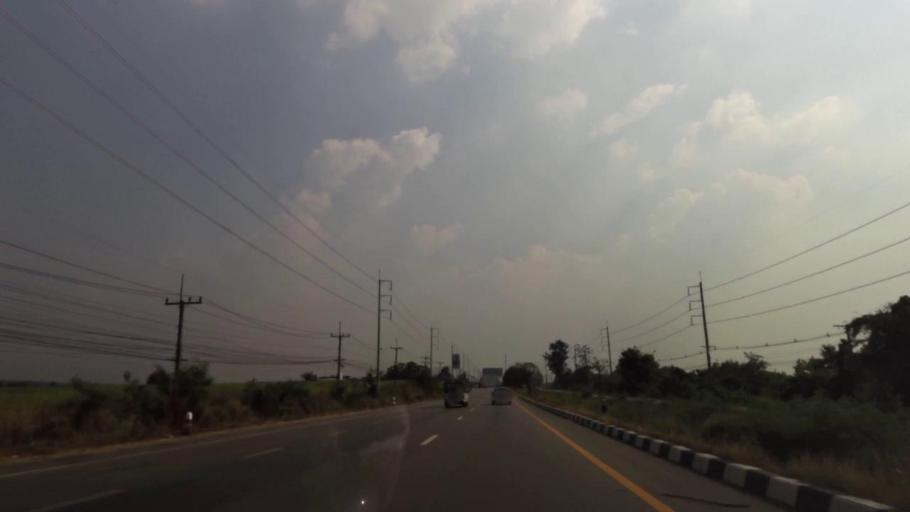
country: TH
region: Chon Buri
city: Nong Yai
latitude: 13.2139
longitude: 101.2407
